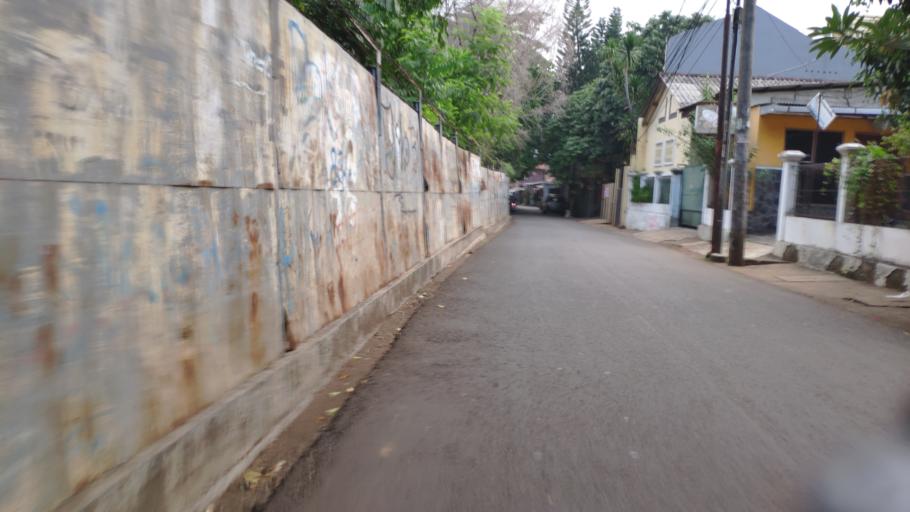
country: ID
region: Jakarta Raya
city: Jakarta
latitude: -6.2944
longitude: 106.8118
